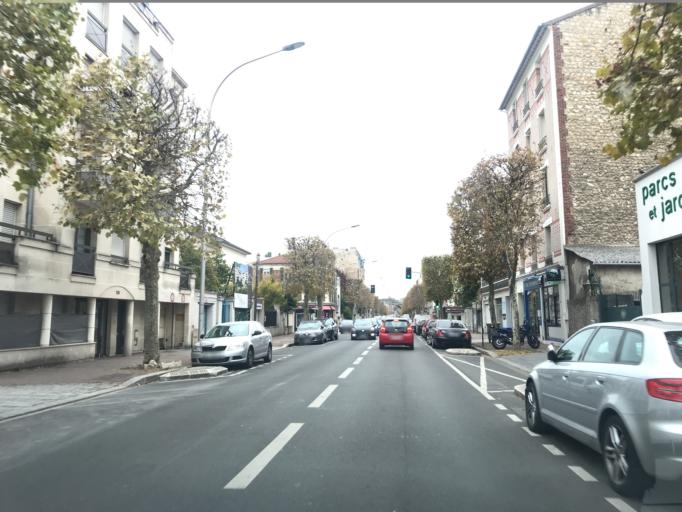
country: FR
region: Ile-de-France
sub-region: Departement du Val-de-Marne
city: Le Perreux-sur-Marne
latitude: 48.8349
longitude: 2.5053
